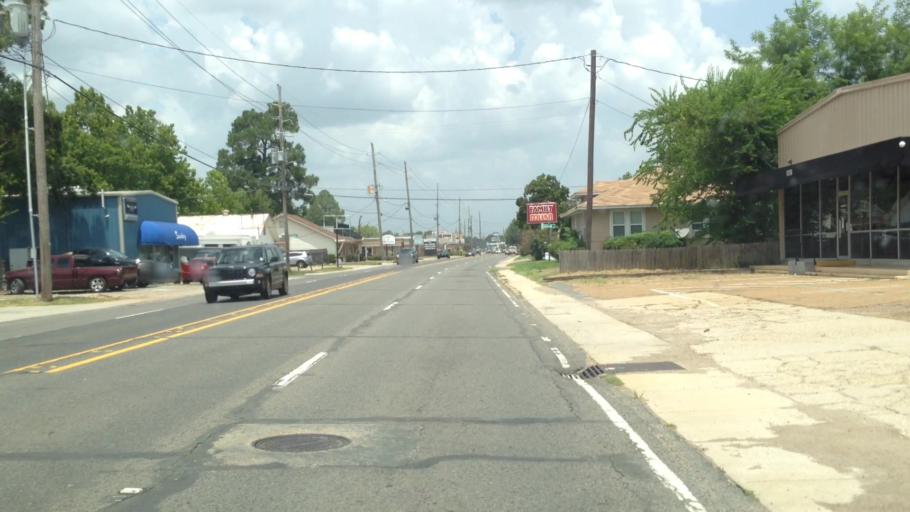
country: US
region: Louisiana
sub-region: Ouachita Parish
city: Monroe
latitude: 32.5088
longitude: -92.1327
